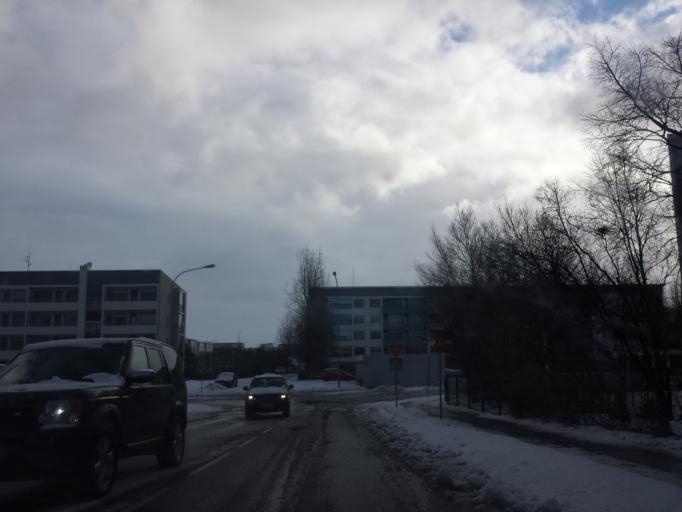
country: IS
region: Capital Region
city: Reykjavik
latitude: 64.1373
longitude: -21.8983
